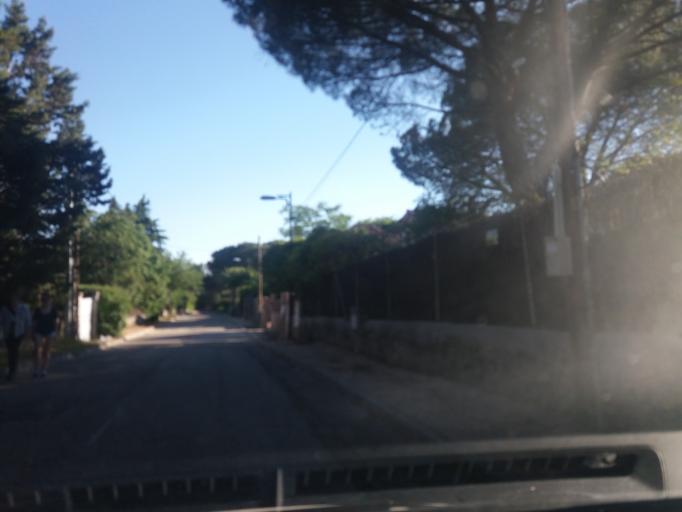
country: ES
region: Madrid
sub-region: Provincia de Madrid
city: Torrelodones
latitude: 40.5847
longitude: -3.9581
